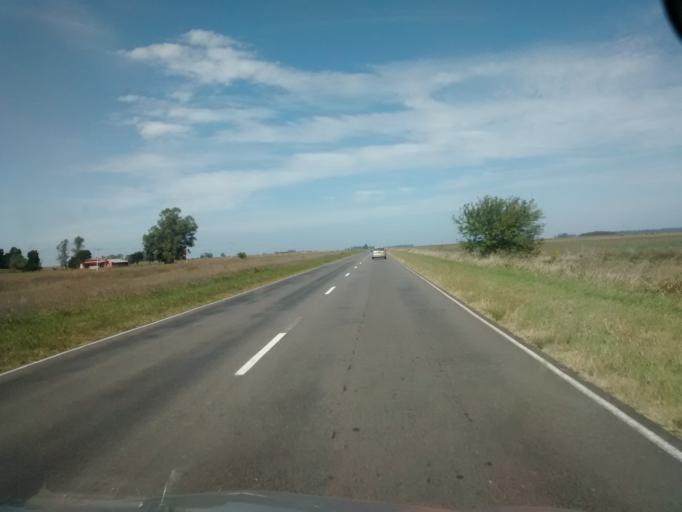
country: AR
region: Buenos Aires
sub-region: Partido de Ayacucho
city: Ayacucho
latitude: -36.6607
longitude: -58.5742
